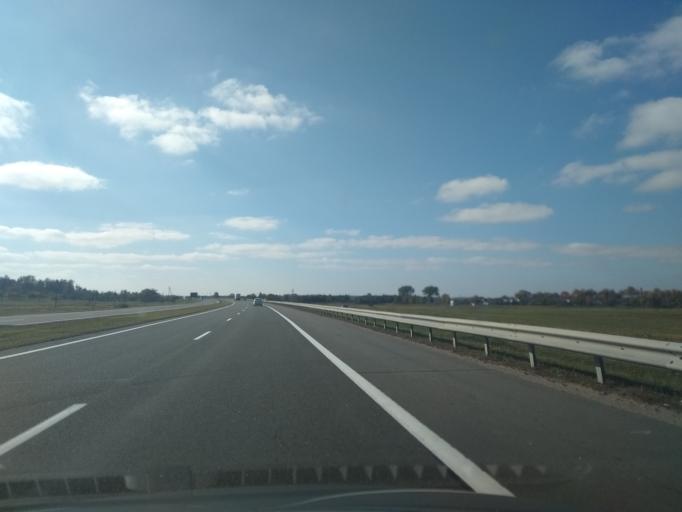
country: BY
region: Brest
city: Baranovichi
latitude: 53.1369
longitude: 25.9263
